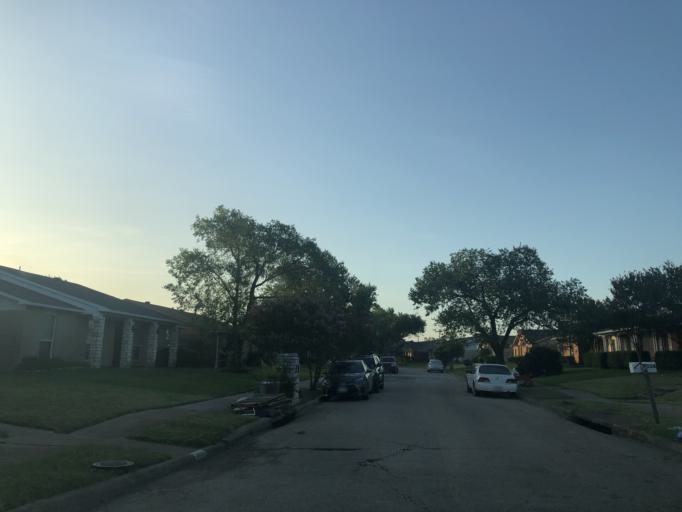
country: US
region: Texas
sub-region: Dallas County
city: Duncanville
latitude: 32.6445
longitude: -96.9551
